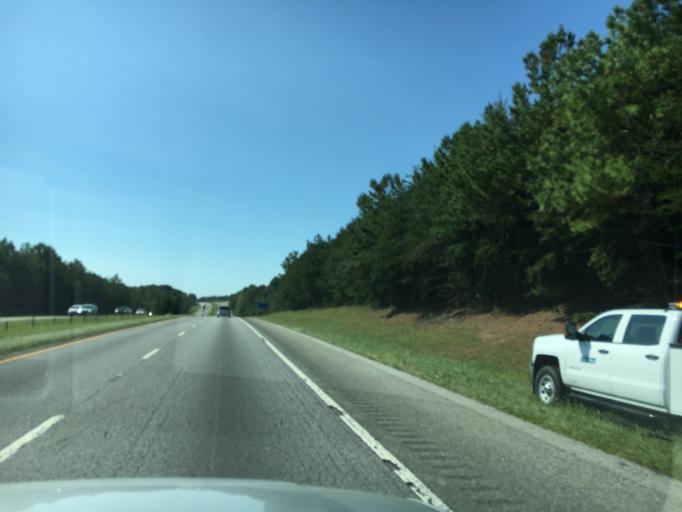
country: US
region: South Carolina
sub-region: Spartanburg County
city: Woodruff
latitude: 34.7583
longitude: -81.9544
